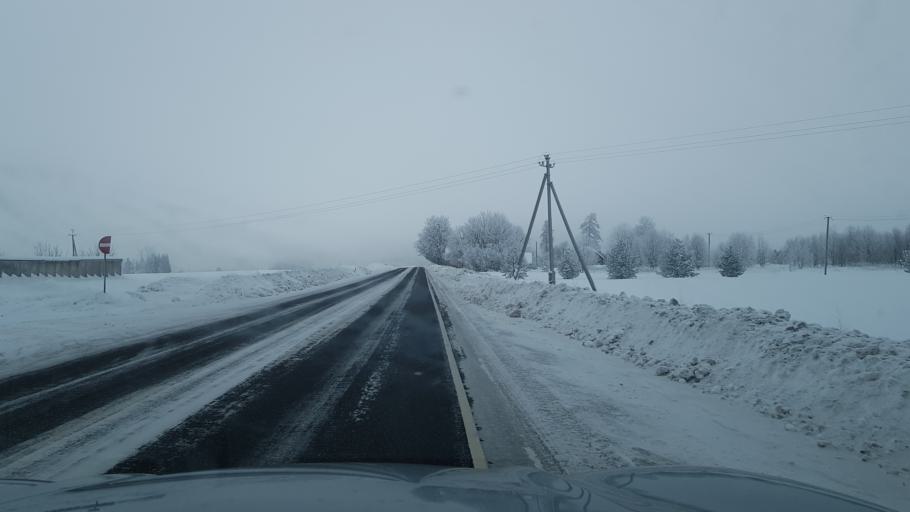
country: EE
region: Ida-Virumaa
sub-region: Johvi vald
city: Johvi
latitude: 59.2608
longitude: 27.3839
